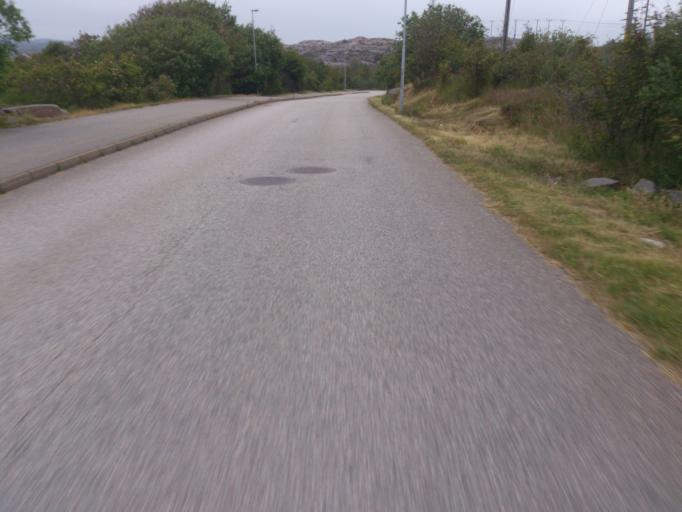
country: SE
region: Vaestra Goetaland
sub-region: Sotenas Kommun
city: Kungshamn
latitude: 58.3760
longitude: 11.2662
